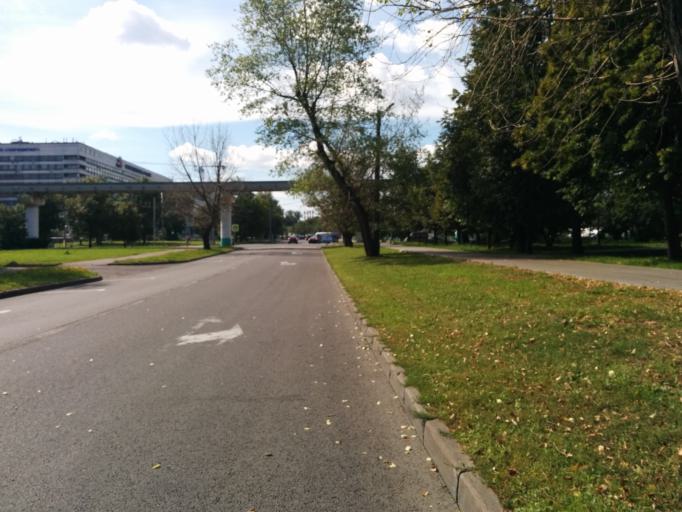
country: RU
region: Moscow
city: Ostankinskiy
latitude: 55.8226
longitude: 37.6167
